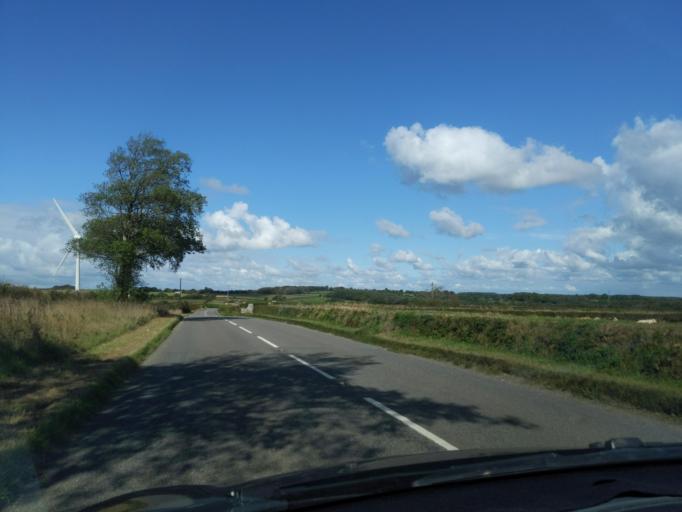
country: GB
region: England
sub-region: Cornwall
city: Boyton
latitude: 50.7385
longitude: -4.3227
